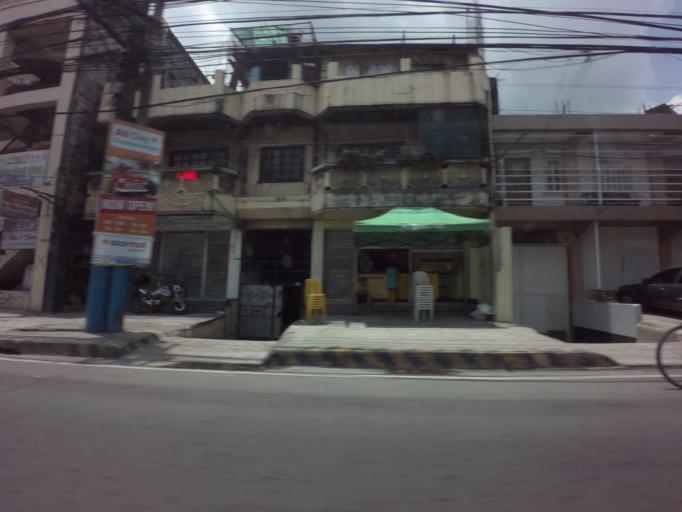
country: PH
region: Calabarzon
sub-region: Province of Laguna
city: San Pedro
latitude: 14.4028
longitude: 121.0472
